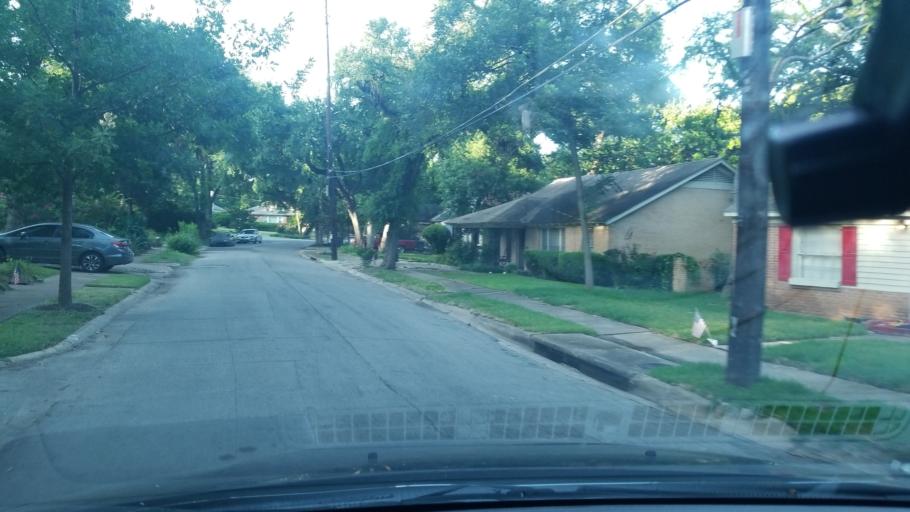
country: US
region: Texas
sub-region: Dallas County
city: Dallas
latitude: 32.7308
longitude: -96.8205
